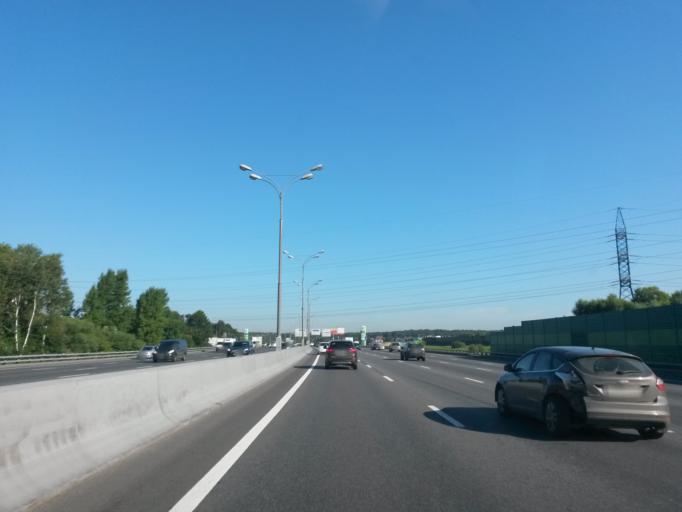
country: RU
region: Moscow
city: Gol'yanovo
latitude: 55.8231
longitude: 37.8363
